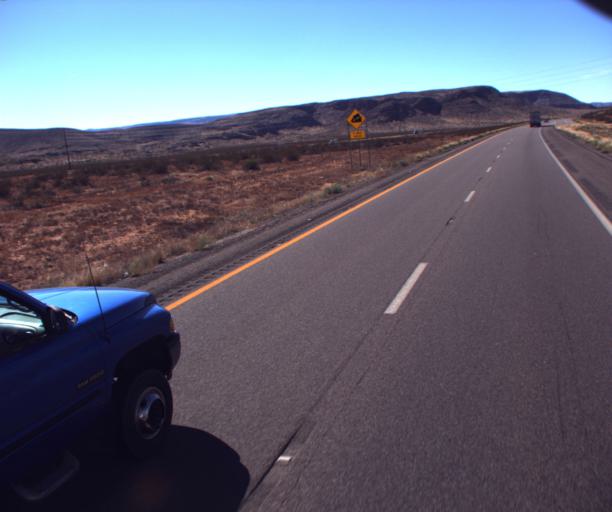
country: US
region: Utah
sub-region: Washington County
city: Saint George
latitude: 36.9828
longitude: -113.6463
